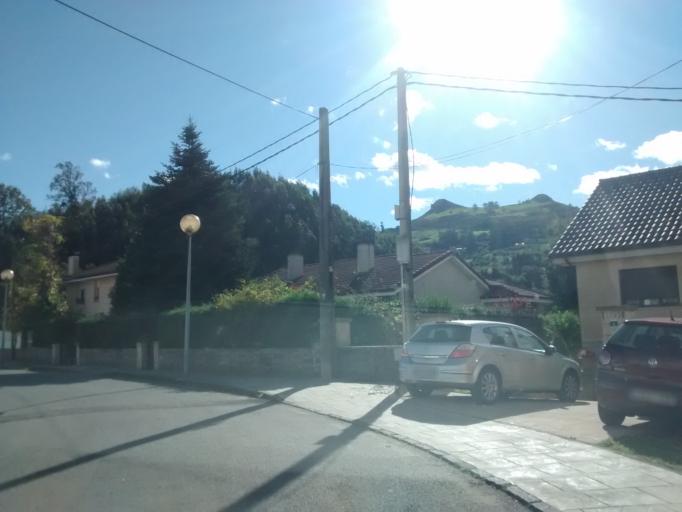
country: ES
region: Cantabria
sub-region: Provincia de Cantabria
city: Lierganes
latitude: 43.3448
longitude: -3.7427
